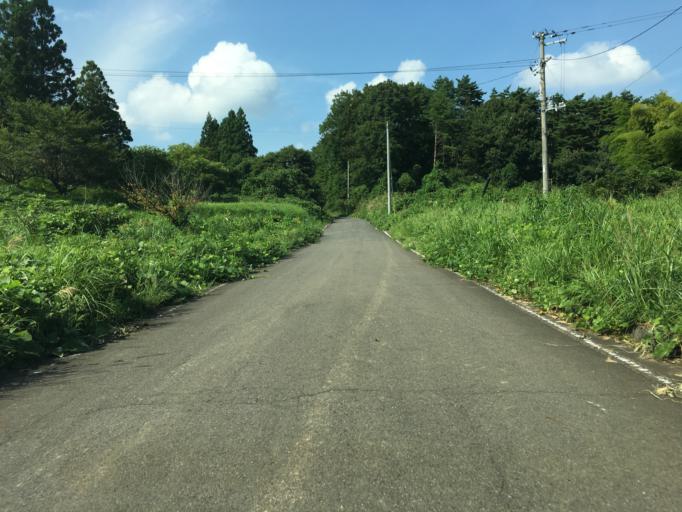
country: JP
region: Fukushima
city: Nihommatsu
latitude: 37.6068
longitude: 140.3852
